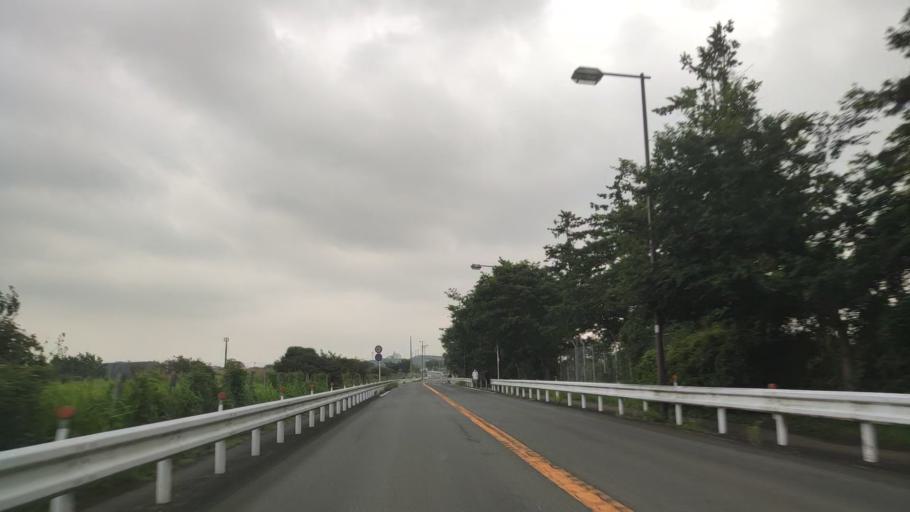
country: JP
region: Kanagawa
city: Fujisawa
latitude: 35.3997
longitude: 139.5029
